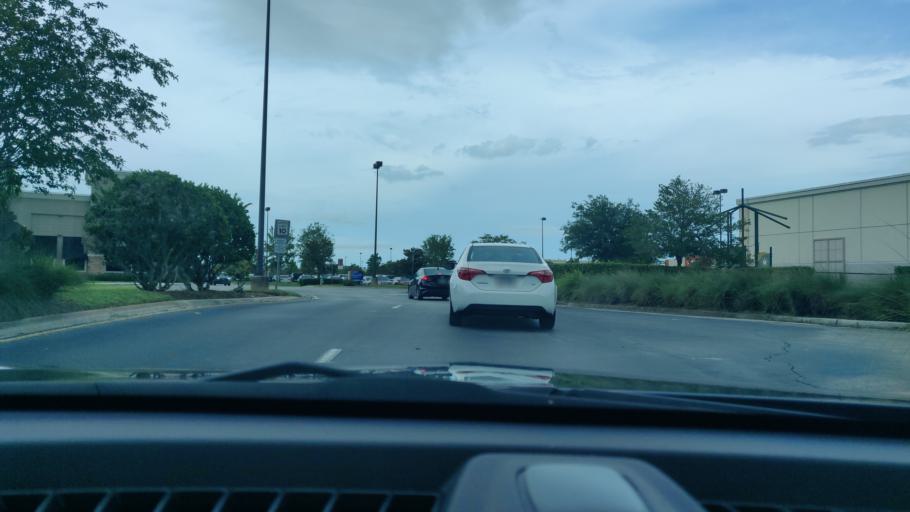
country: US
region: Florida
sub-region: Orange County
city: Hunters Creek
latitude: 28.3434
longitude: -81.4305
